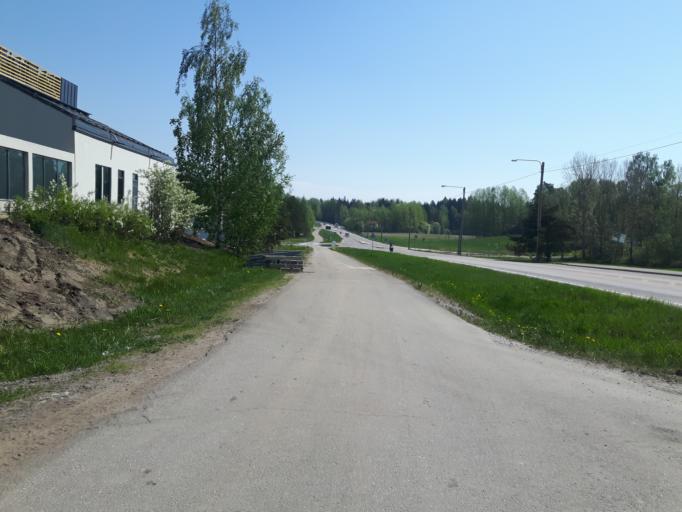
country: FI
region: Uusimaa
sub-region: Helsinki
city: Nickby
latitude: 60.2979
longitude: 25.3412
